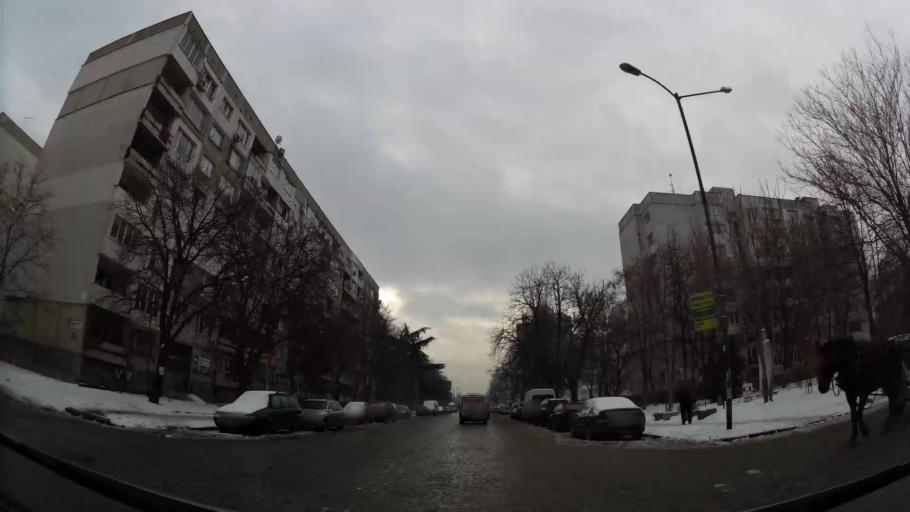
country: BG
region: Sofia-Capital
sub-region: Stolichna Obshtina
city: Sofia
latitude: 42.7132
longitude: 23.2990
